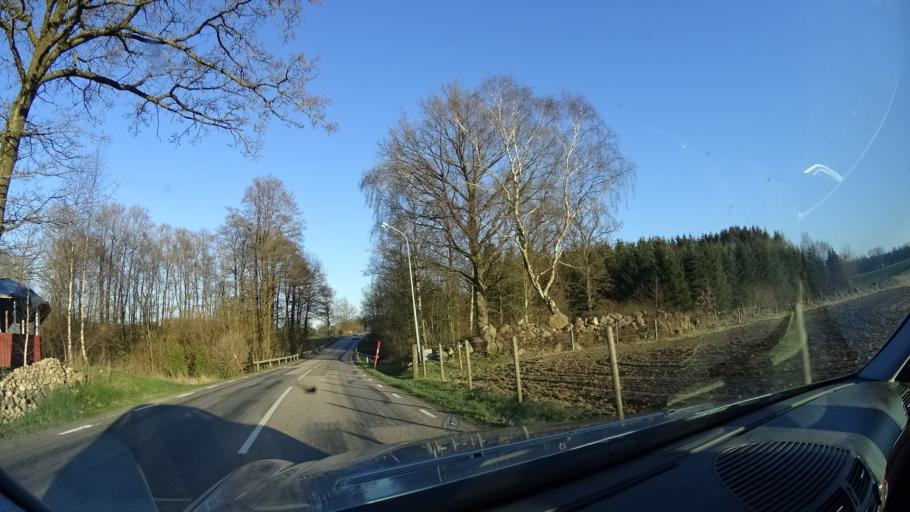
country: SE
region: Skane
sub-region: Svalovs Kommun
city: Kagerod
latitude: 56.0103
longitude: 13.0722
